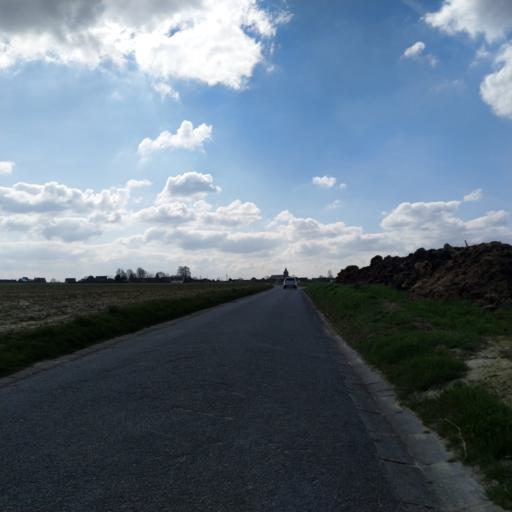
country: BE
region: Wallonia
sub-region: Province du Hainaut
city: Lens
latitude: 50.5718
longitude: 3.9406
